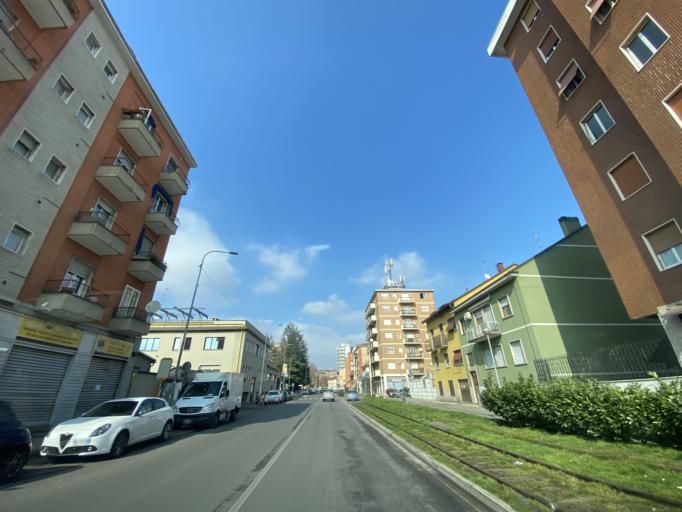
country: IT
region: Lombardy
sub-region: Citta metropolitana di Milano
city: Bresso
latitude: 45.5319
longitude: 9.1932
